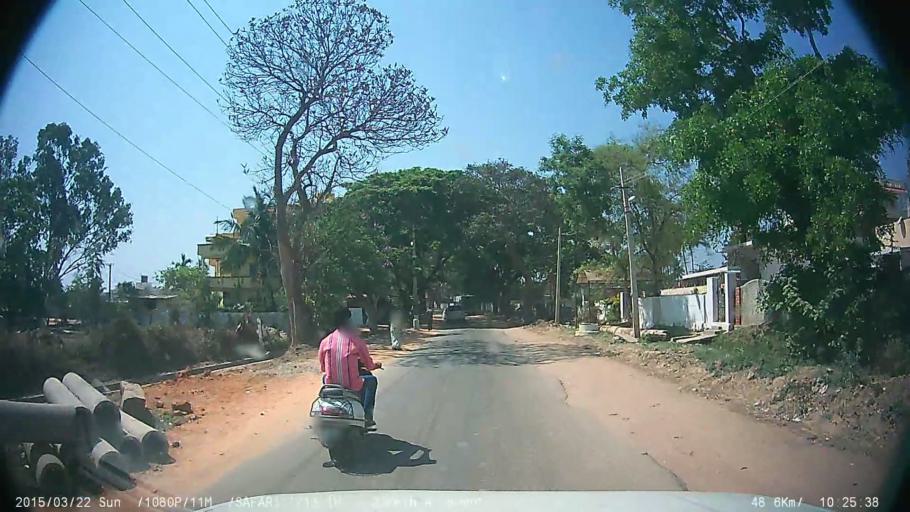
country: IN
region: Karnataka
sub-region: Bangalore Urban
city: Anekal
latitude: 12.8099
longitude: 77.5785
